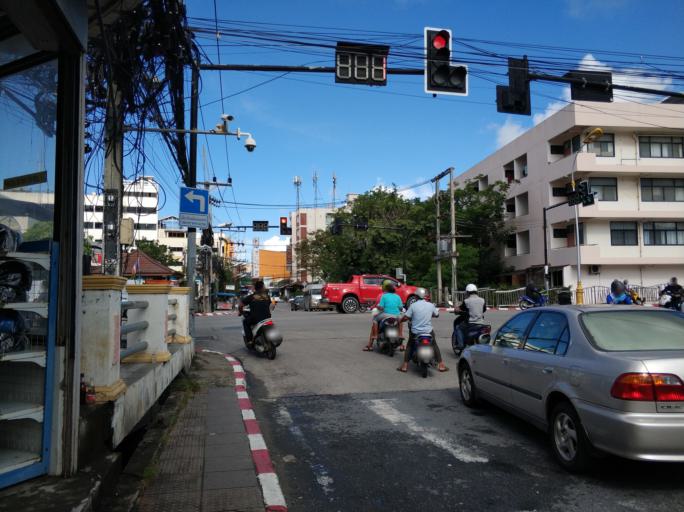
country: TH
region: Phuket
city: Patong
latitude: 7.8965
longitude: 98.3023
